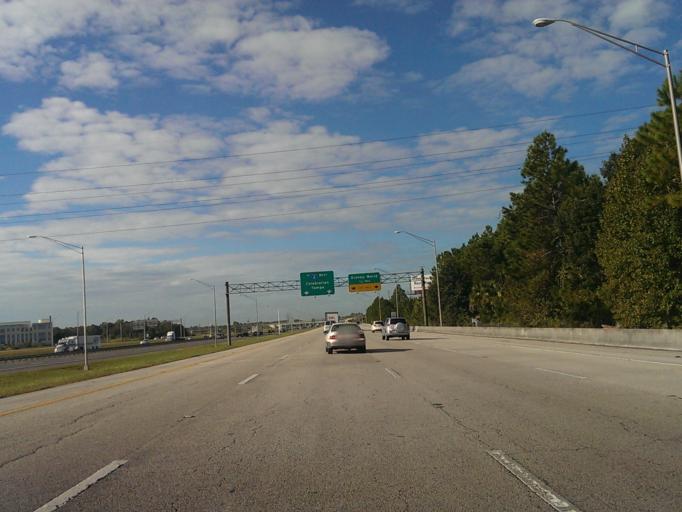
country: US
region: Florida
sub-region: Osceola County
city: Celebration
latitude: 28.3146
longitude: -81.5632
